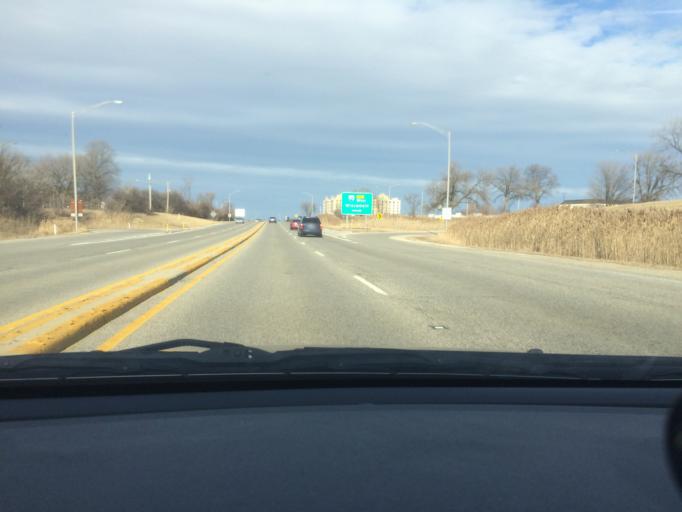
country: US
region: Illinois
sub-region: Kane County
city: Sleepy Hollow
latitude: 42.0675
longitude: -88.2914
